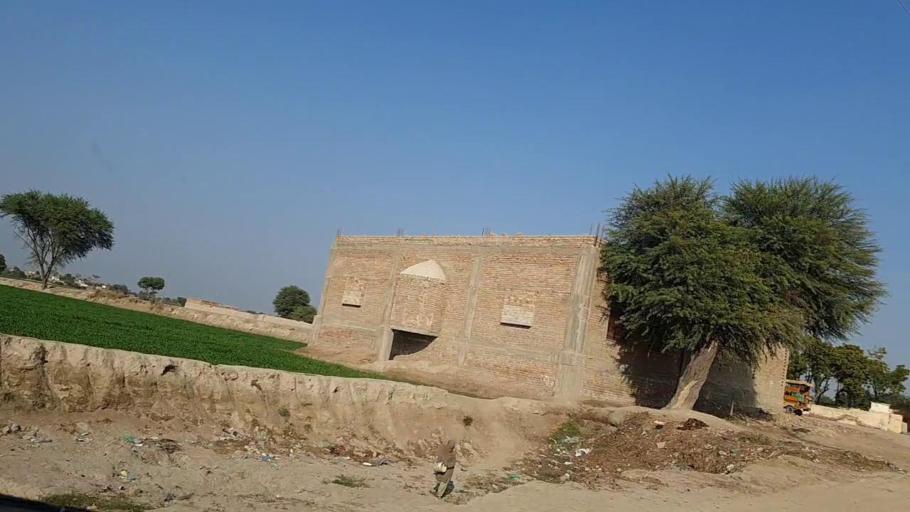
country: PK
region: Sindh
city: Sakrand
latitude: 26.1275
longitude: 68.2378
